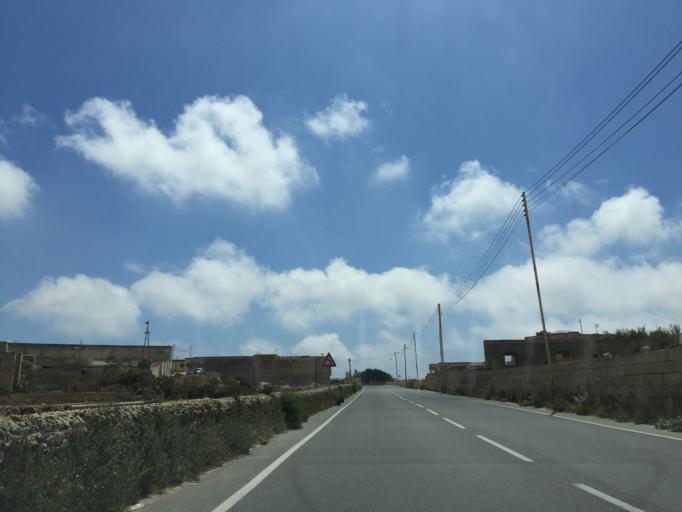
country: MT
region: Ir-Rabat
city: Rabat
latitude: 35.8716
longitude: 14.3924
